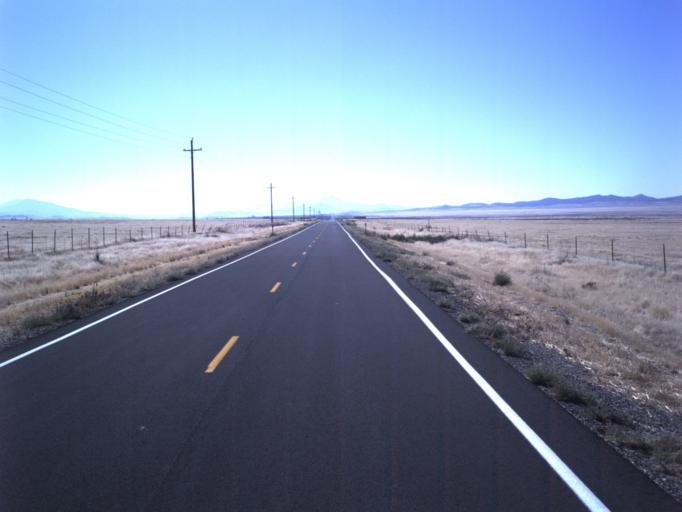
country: US
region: Utah
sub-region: Tooele County
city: Grantsville
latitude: 40.3963
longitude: -112.7477
